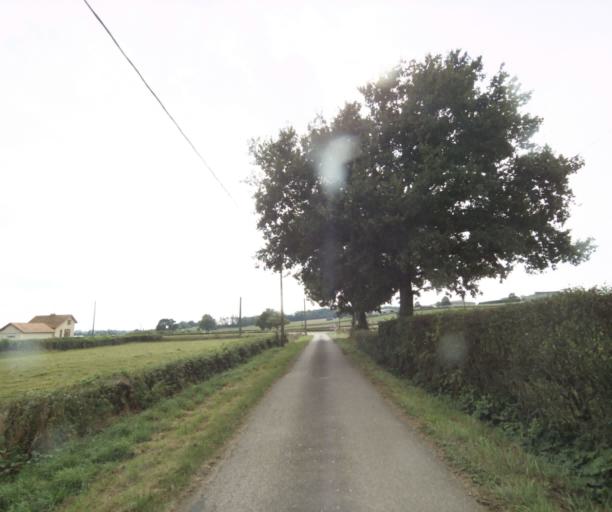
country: FR
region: Bourgogne
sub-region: Departement de Saone-et-Loire
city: Palinges
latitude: 46.5102
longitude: 4.1821
